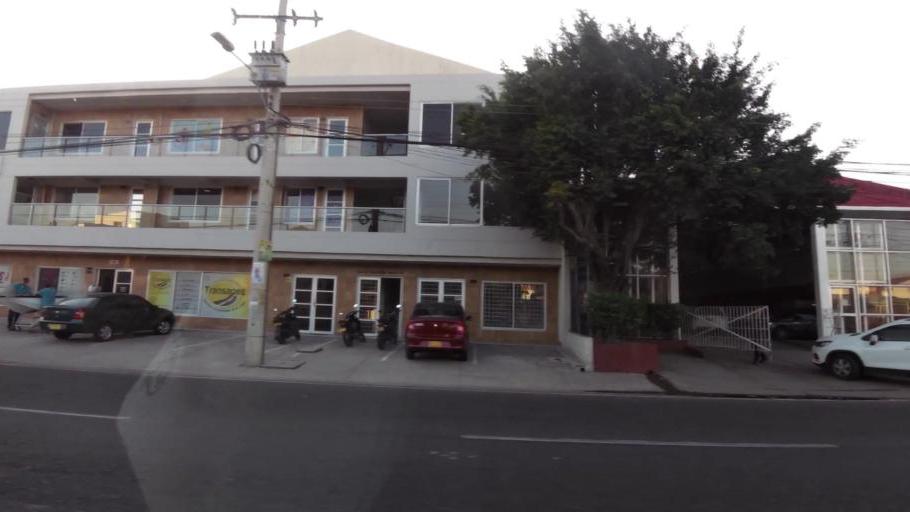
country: CO
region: Bolivar
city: Cartagena
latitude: 10.4029
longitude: -75.5216
